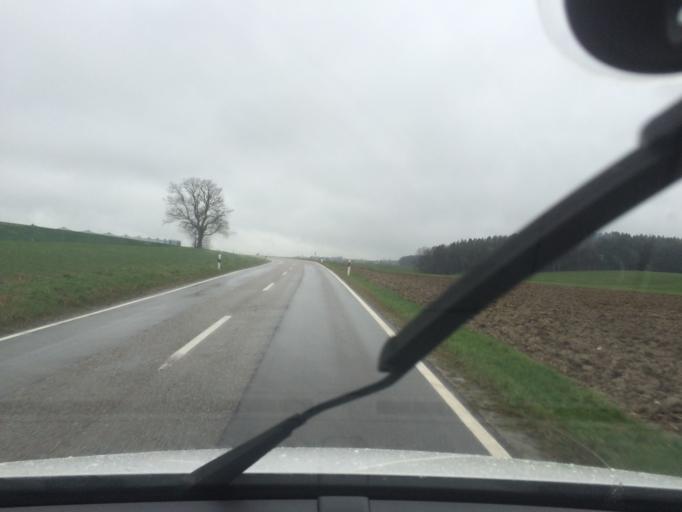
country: DE
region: Bavaria
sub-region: Upper Bavaria
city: Assling
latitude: 47.9592
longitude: 11.9690
